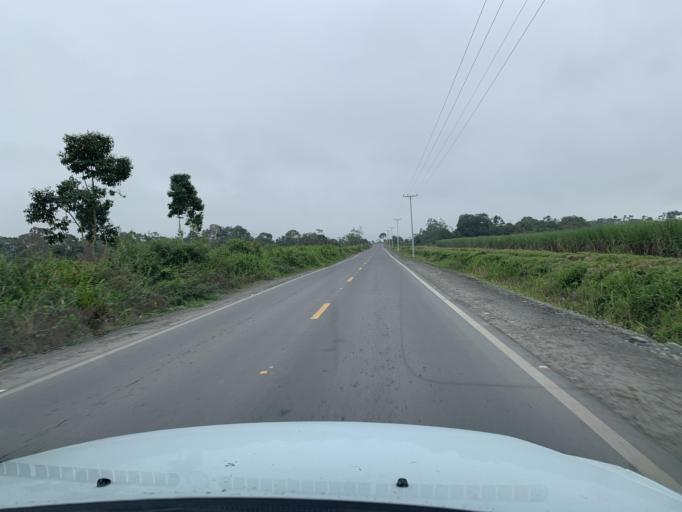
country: EC
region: Guayas
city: Coronel Marcelino Mariduena
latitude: -2.3320
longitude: -79.5268
